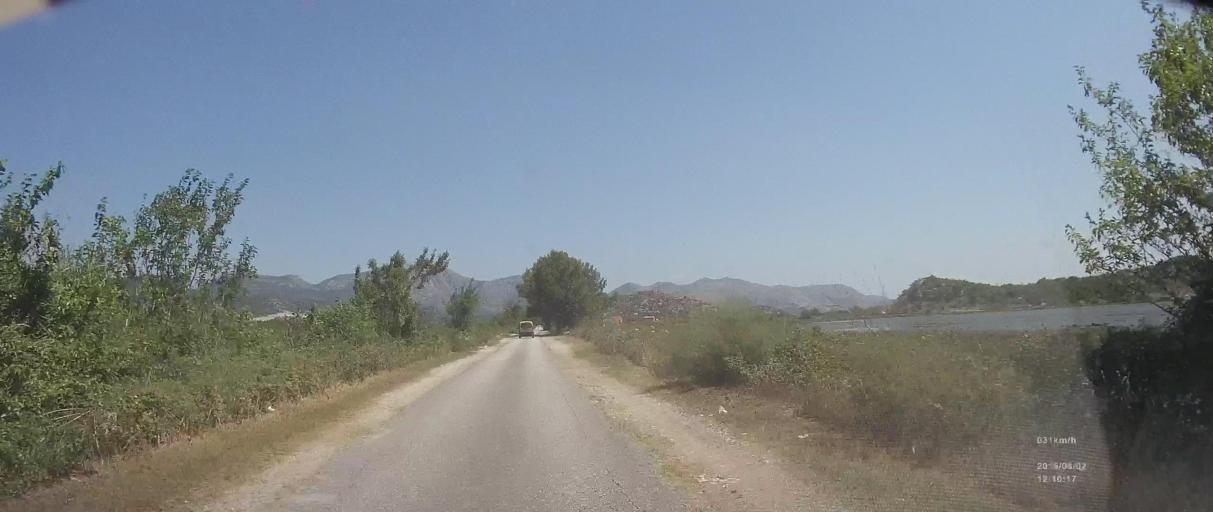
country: HR
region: Dubrovacko-Neretvanska
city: Komin
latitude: 43.0243
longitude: 17.4557
